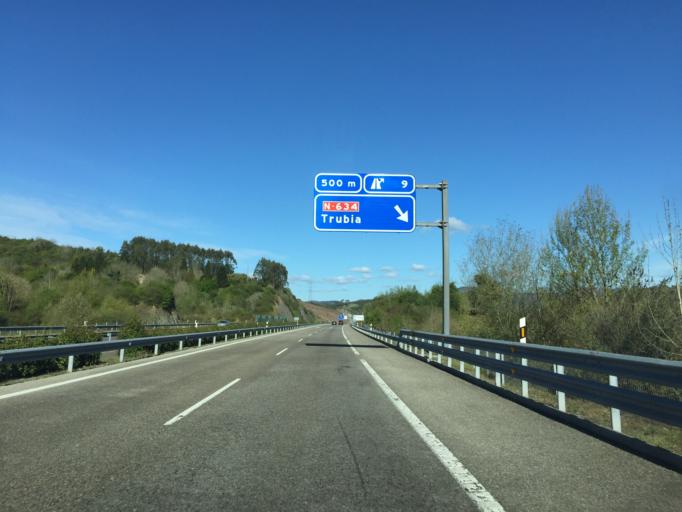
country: ES
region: Asturias
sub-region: Province of Asturias
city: Castandiello
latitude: 43.3565
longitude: -5.9399
